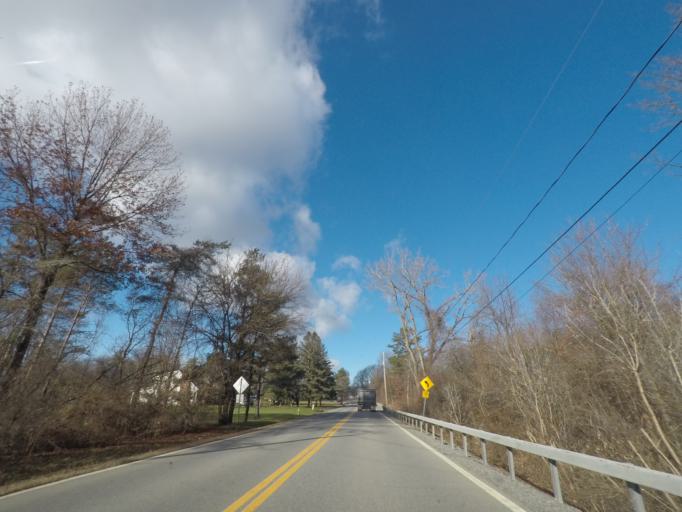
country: US
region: New York
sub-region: Saratoga County
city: Waterford
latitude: 42.8334
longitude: -73.6897
